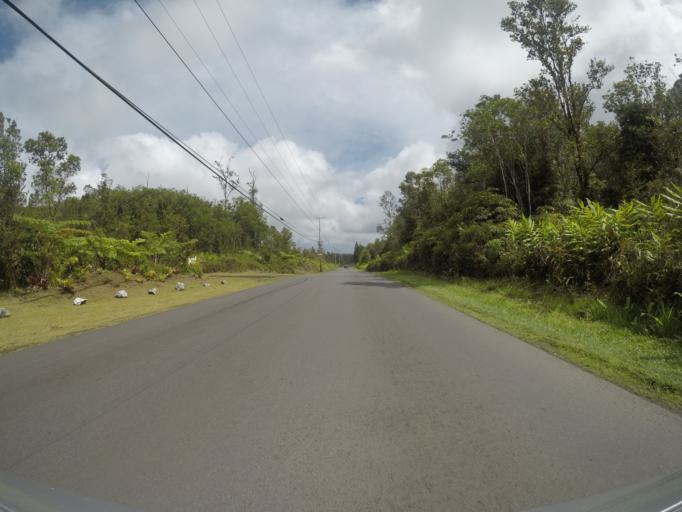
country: US
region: Hawaii
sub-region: Hawaii County
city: Fern Acres
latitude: 19.4759
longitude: -155.1405
